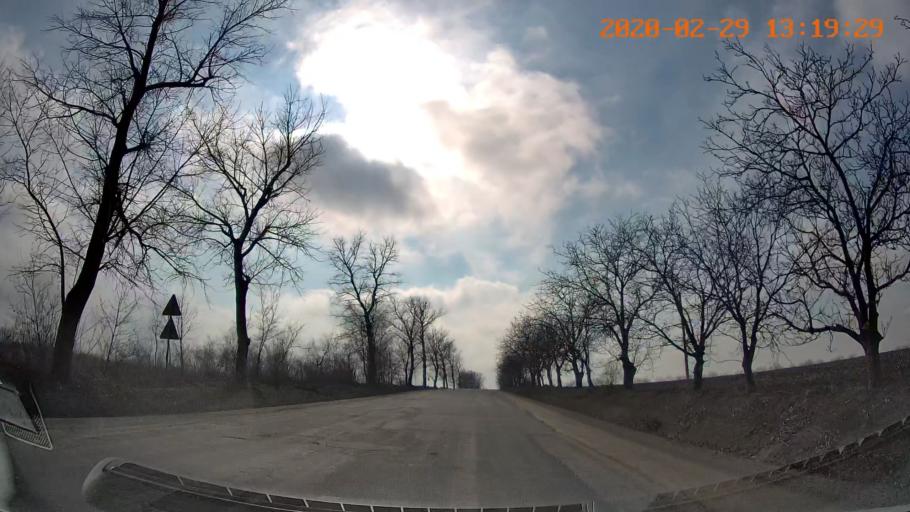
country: MD
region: Telenesti
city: Camenca
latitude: 47.9883
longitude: 28.6506
